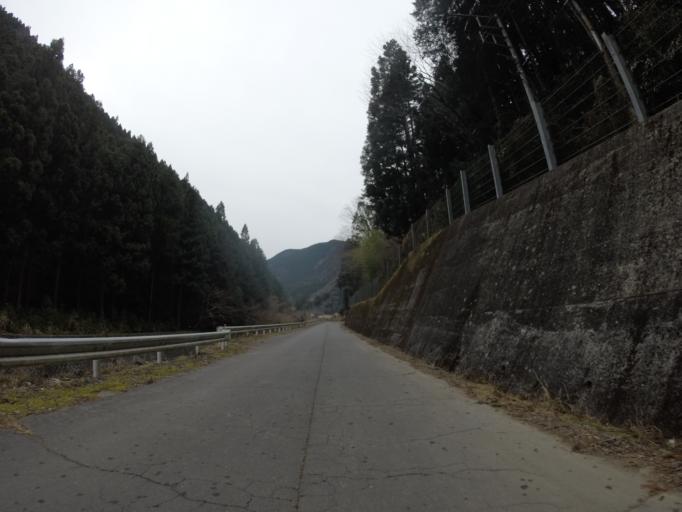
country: JP
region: Shizuoka
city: Fujinomiya
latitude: 35.2822
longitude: 138.5339
